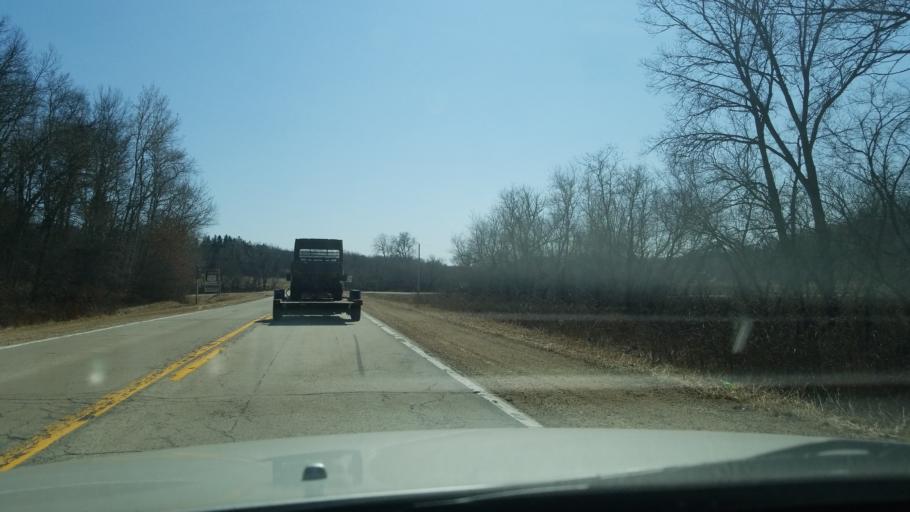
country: US
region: Wisconsin
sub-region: Iowa County
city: Mineral Point
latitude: 42.8699
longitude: -90.2046
